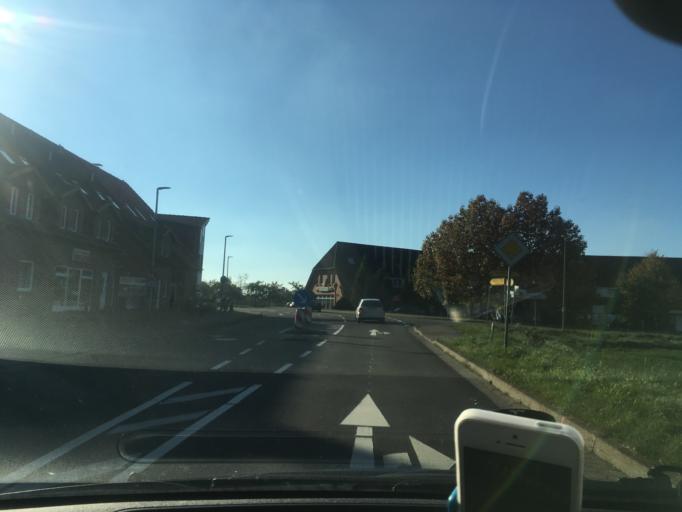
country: DE
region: Mecklenburg-Vorpommern
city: Dummer
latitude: 53.5658
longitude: 11.2075
